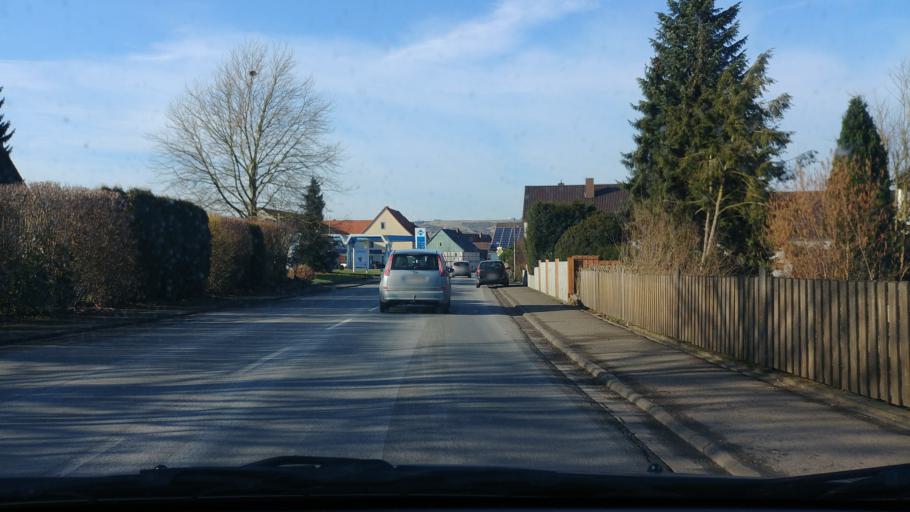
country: DE
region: Hesse
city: Trendelburg
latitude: 51.5898
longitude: 9.4103
